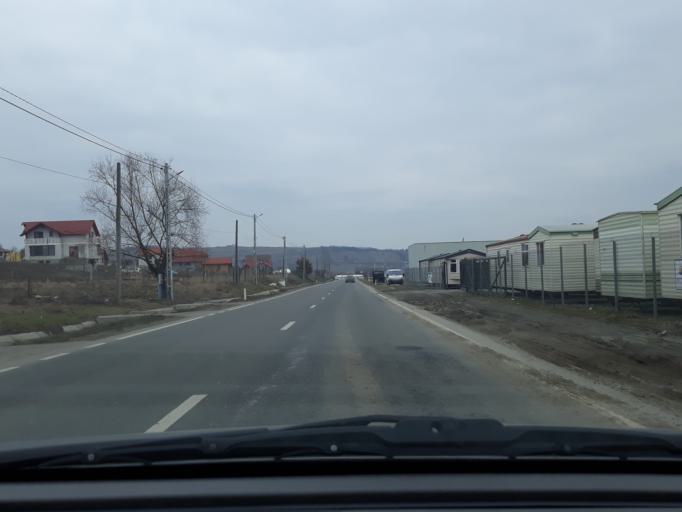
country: RO
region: Salaj
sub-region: Comuna Hereclean
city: Hereclean
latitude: 47.2351
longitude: 22.9822
